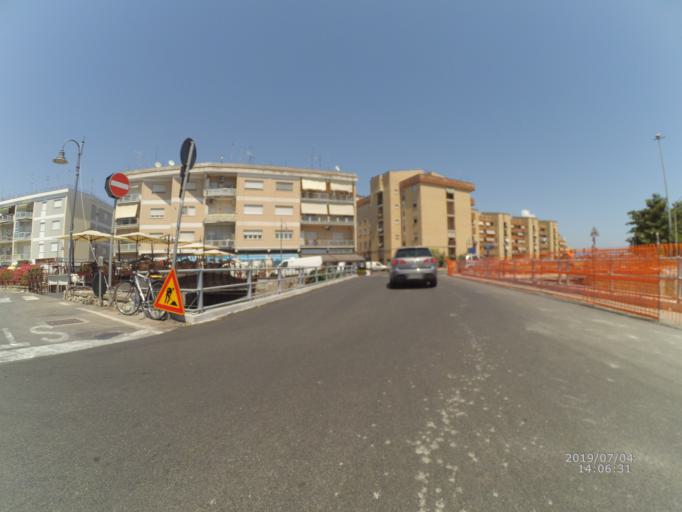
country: IT
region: Latium
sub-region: Provincia di Latina
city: Terracina
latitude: 41.2861
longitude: 13.2533
